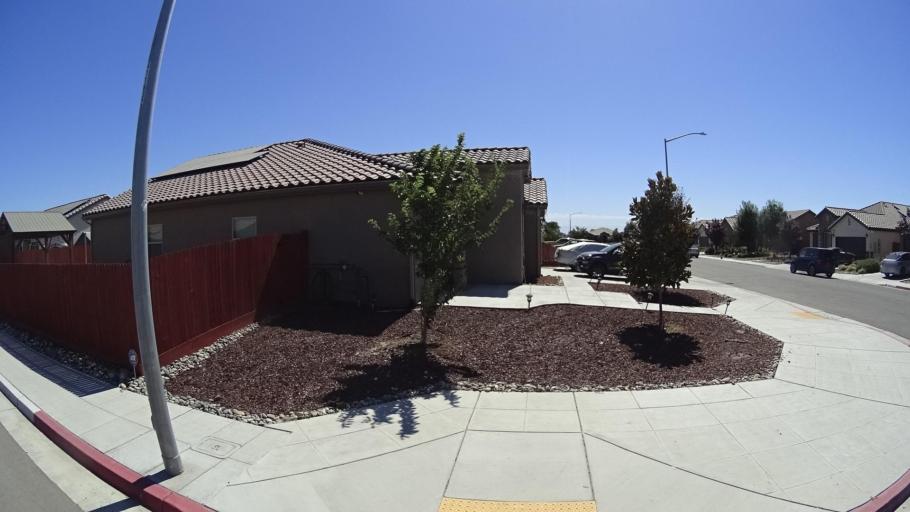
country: US
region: California
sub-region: Fresno County
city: Sunnyside
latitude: 36.7172
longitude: -119.6707
